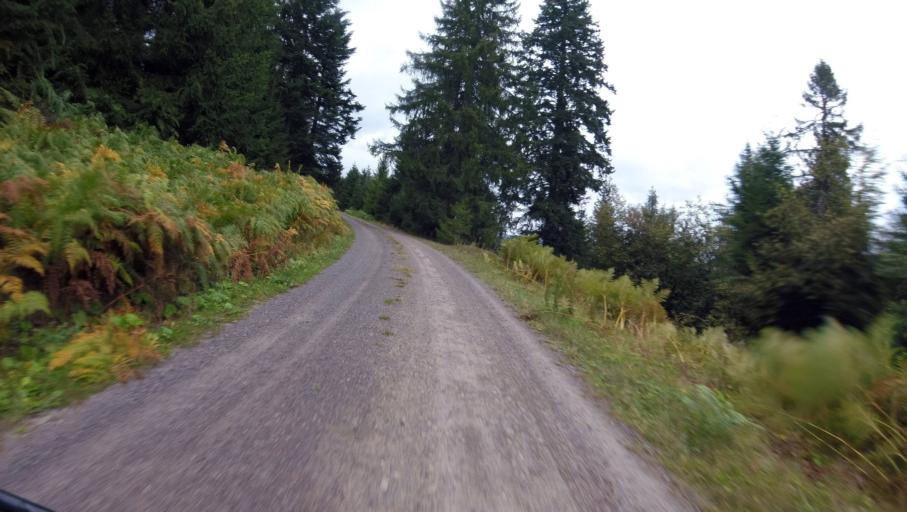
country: DE
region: Baden-Wuerttemberg
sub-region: Karlsruhe Region
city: Enzklosterle
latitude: 48.6633
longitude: 8.4251
